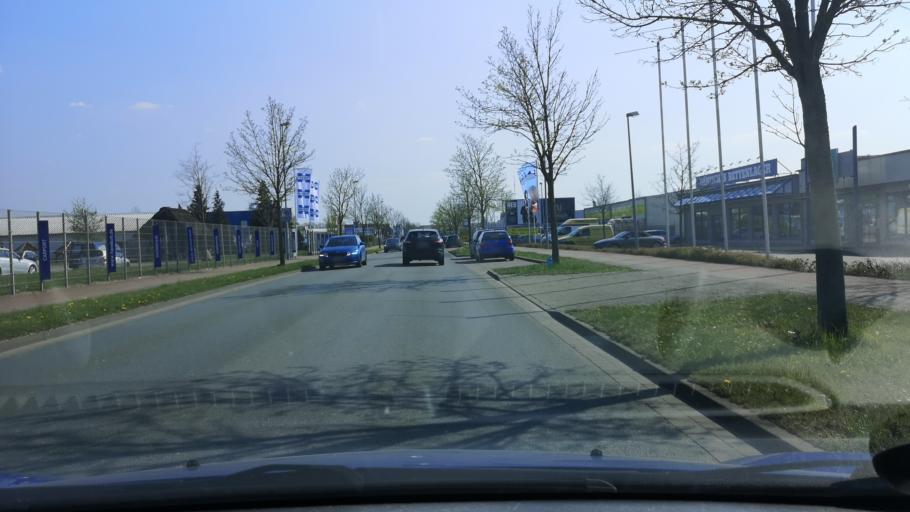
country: DE
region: Lower Saxony
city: Neustadt am Rubenberge
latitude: 52.5080
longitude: 9.4778
